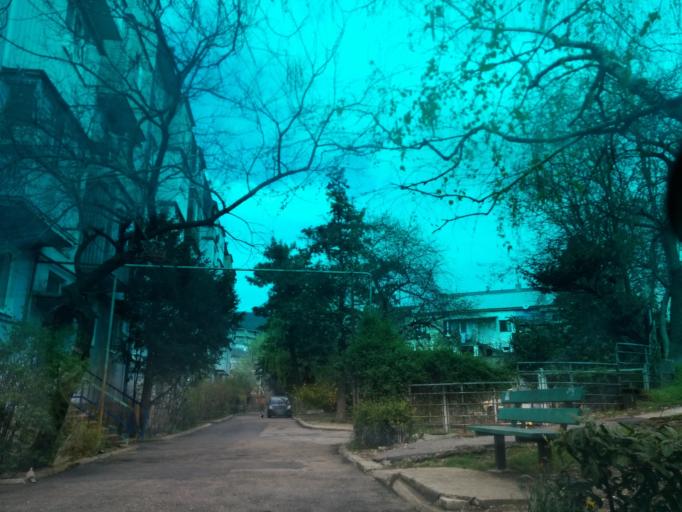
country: RU
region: Krasnodarskiy
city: Tuapse
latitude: 44.1027
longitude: 39.0854
